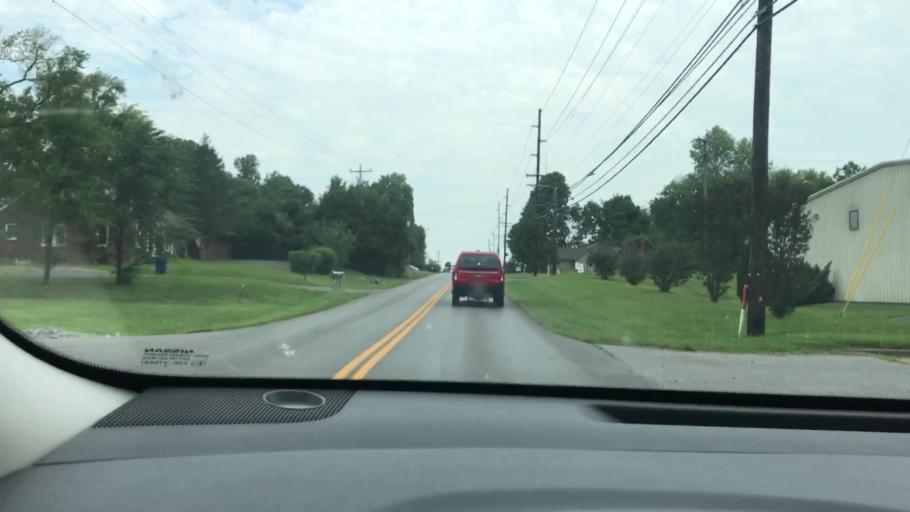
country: US
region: Kentucky
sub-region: Calloway County
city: Murray
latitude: 36.6219
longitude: -88.3020
